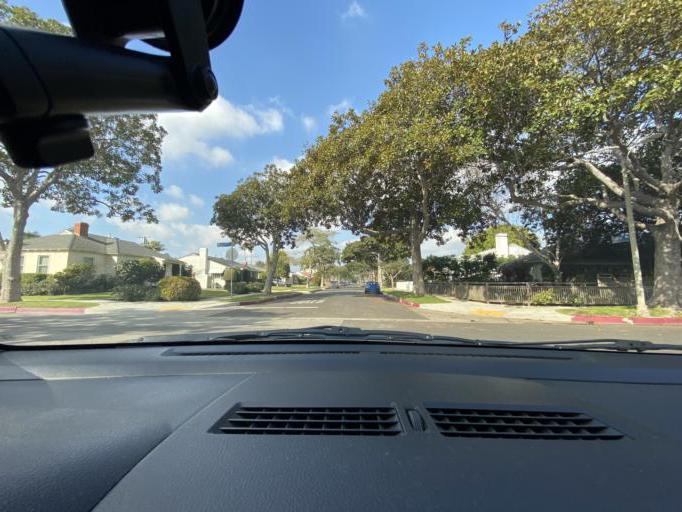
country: US
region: California
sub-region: Los Angeles County
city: Culver City
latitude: 34.0137
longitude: -118.4297
